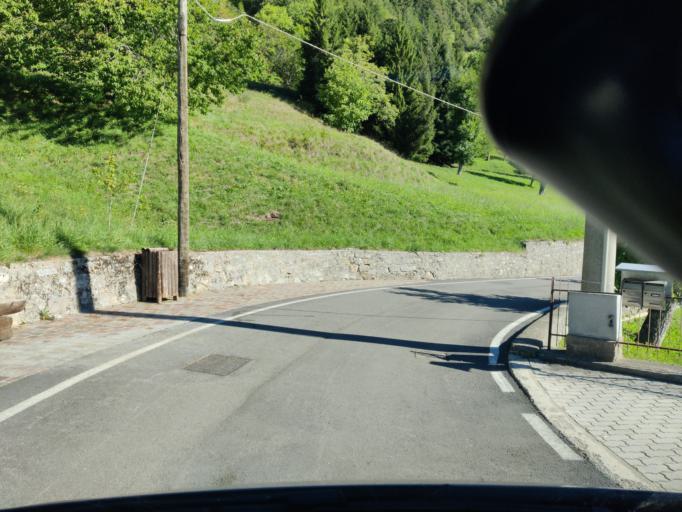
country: IT
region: Lombardy
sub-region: Provincia di Brescia
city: Capovalle
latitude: 45.7551
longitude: 10.5407
